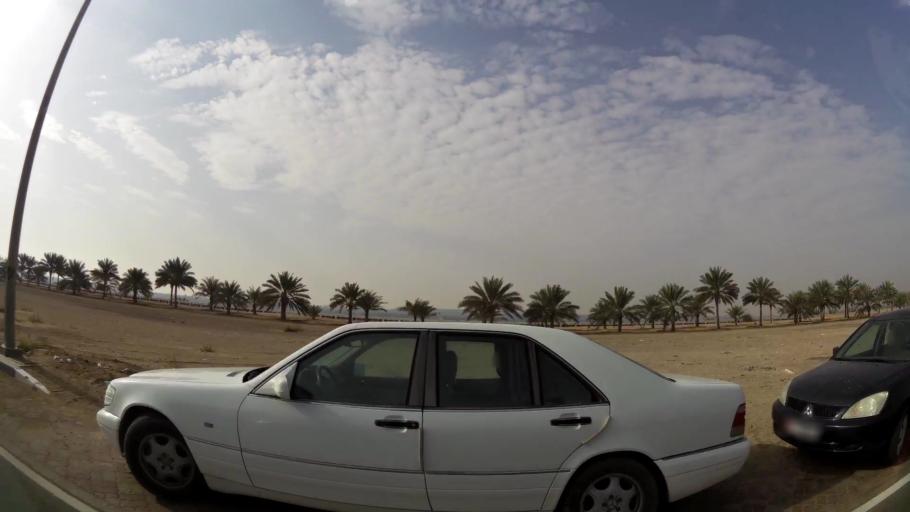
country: AE
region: Abu Dhabi
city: Abu Dhabi
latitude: 24.2410
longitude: 54.7142
